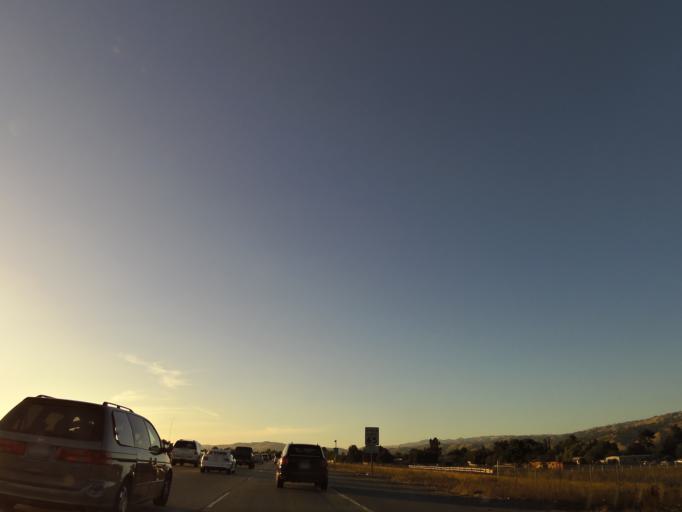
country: US
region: California
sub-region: Santa Clara County
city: San Martin
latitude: 37.0953
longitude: -121.6028
